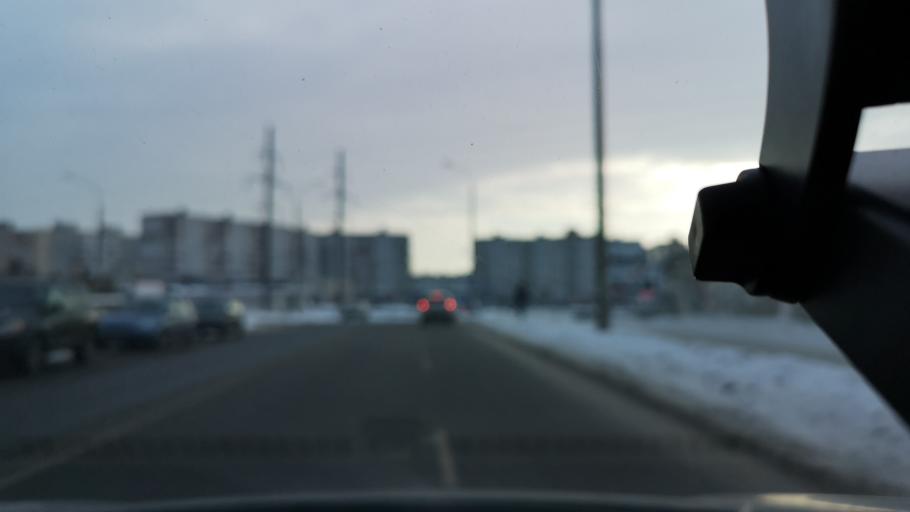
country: BY
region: Minsk
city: Borovlyany
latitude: 53.9533
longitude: 27.6800
